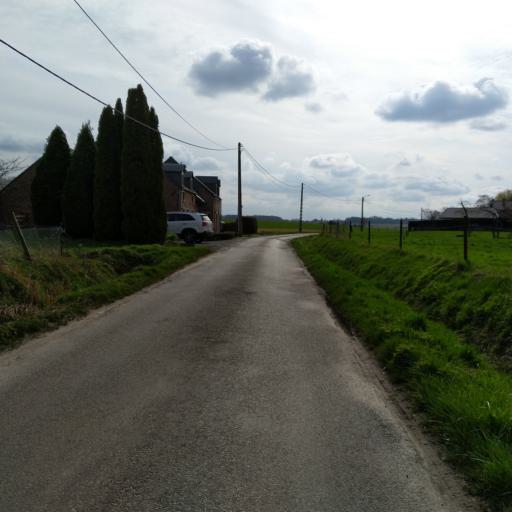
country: BE
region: Wallonia
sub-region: Province du Hainaut
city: Soignies
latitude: 50.5390
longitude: 4.0616
